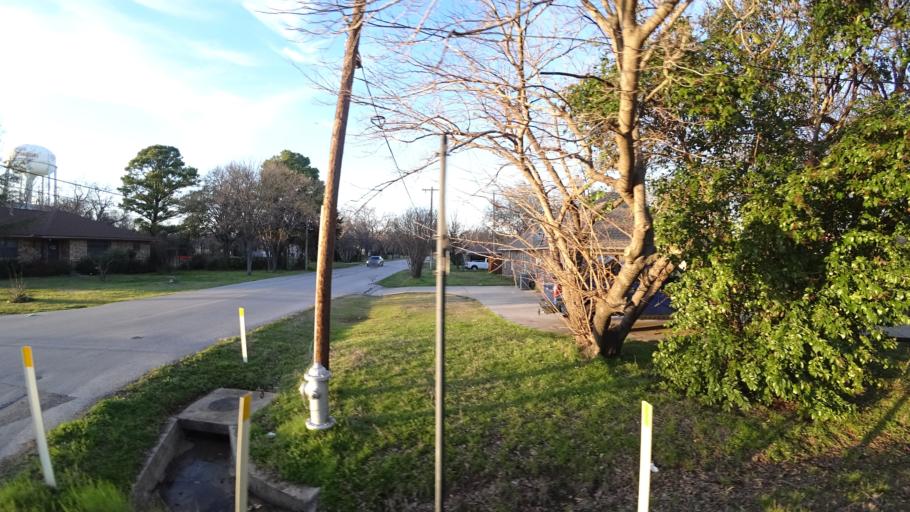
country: US
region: Texas
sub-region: Denton County
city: Lewisville
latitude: 33.0477
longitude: -97.0069
